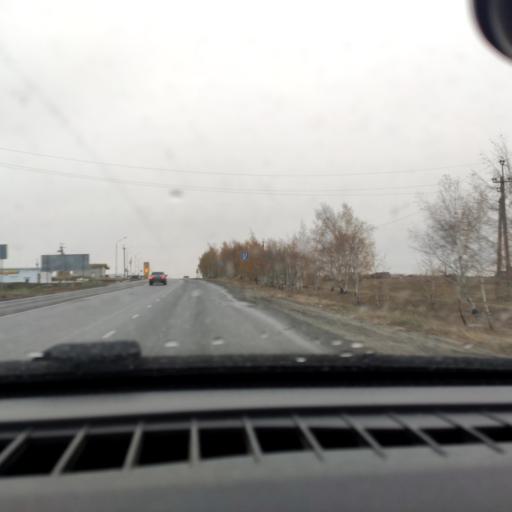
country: RU
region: Belgorod
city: Alekseyevka
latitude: 50.6446
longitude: 38.6831
